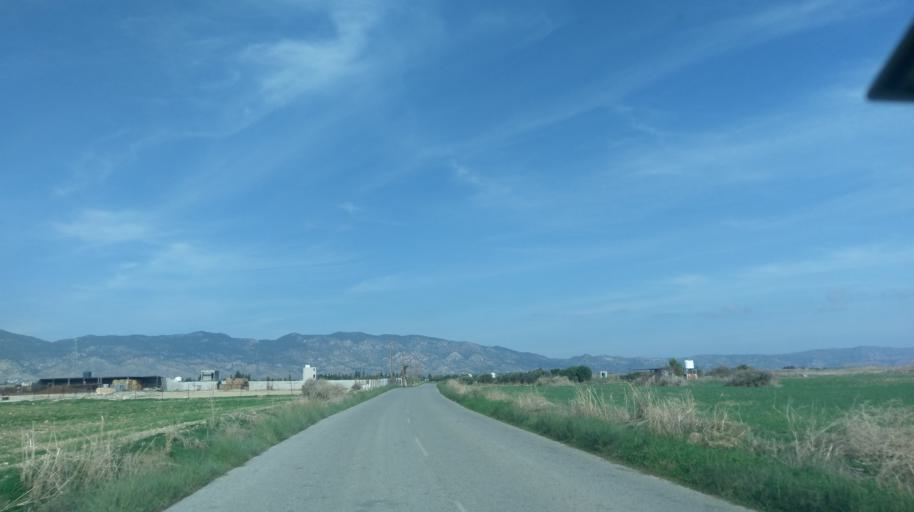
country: CY
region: Ammochostos
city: Lefkonoiko
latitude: 35.2372
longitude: 33.6111
